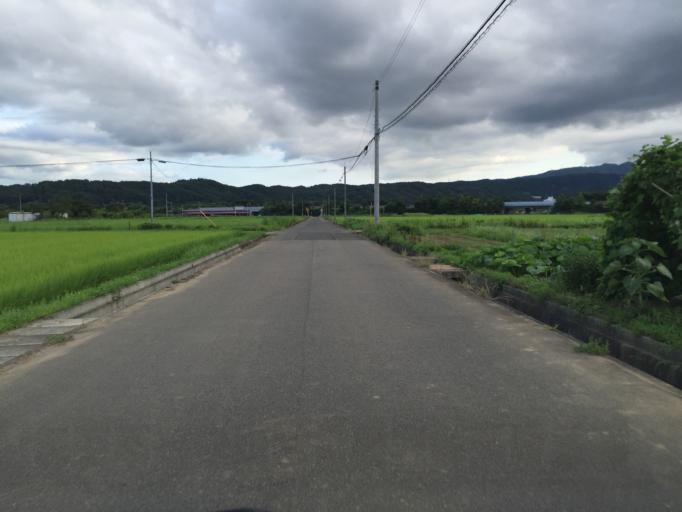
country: JP
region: Fukushima
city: Fukushima-shi
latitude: 37.7208
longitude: 140.4376
